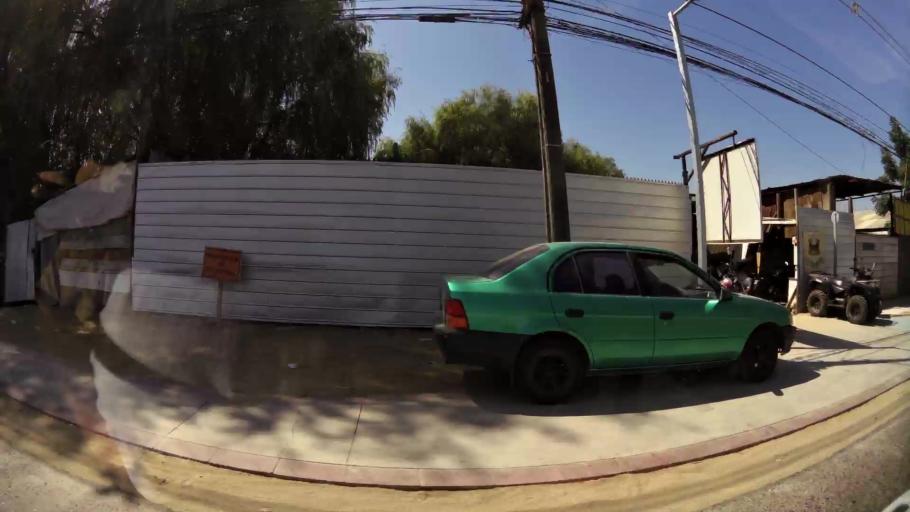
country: CL
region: Maule
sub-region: Provincia de Talca
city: Talca
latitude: -35.4254
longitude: -71.6383
